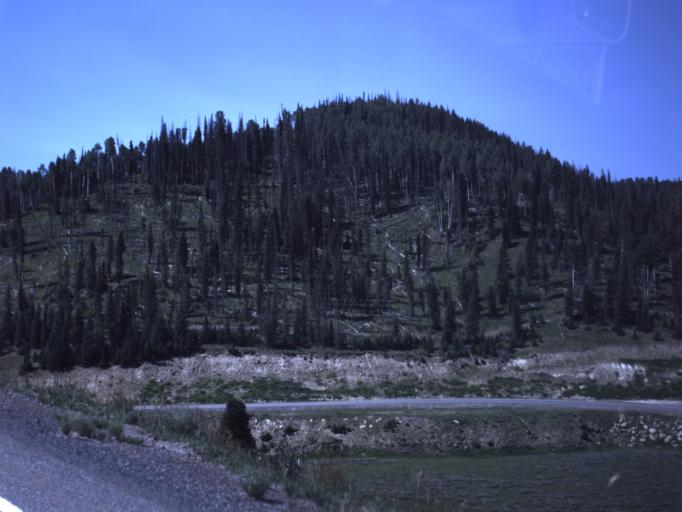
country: US
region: Utah
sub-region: Sanpete County
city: Fairview
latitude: 39.6859
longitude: -111.2448
